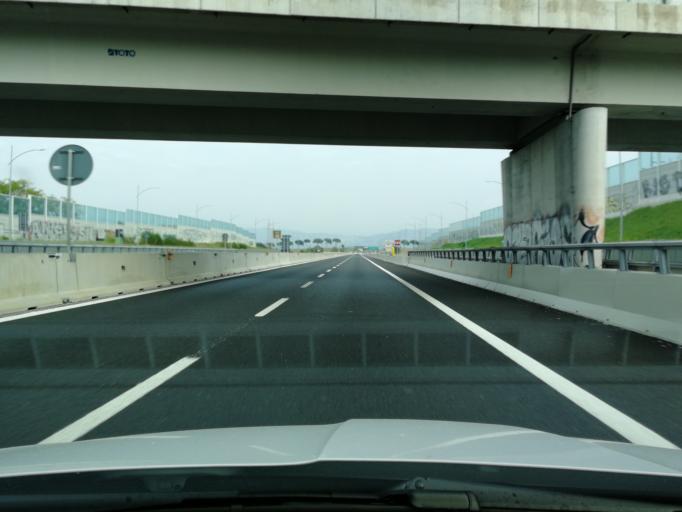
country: IT
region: Latium
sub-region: Citta metropolitana di Roma Capitale
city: Albuccione
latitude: 41.9232
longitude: 12.6832
